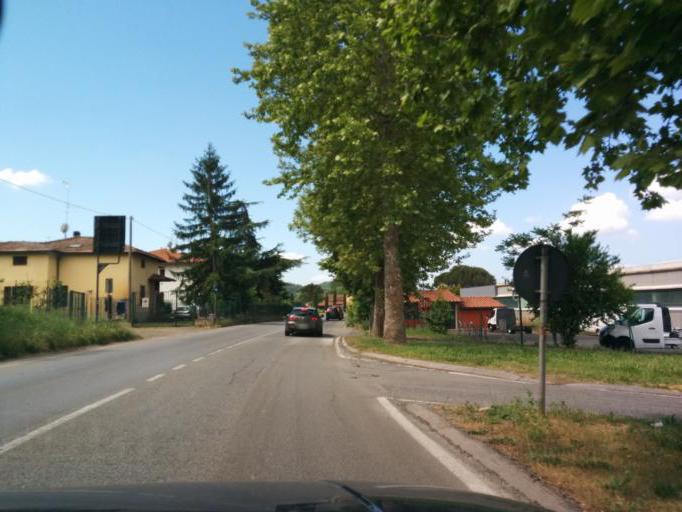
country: IT
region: Tuscany
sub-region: Provincia di Siena
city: Poggibonsi
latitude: 43.4628
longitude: 11.1231
